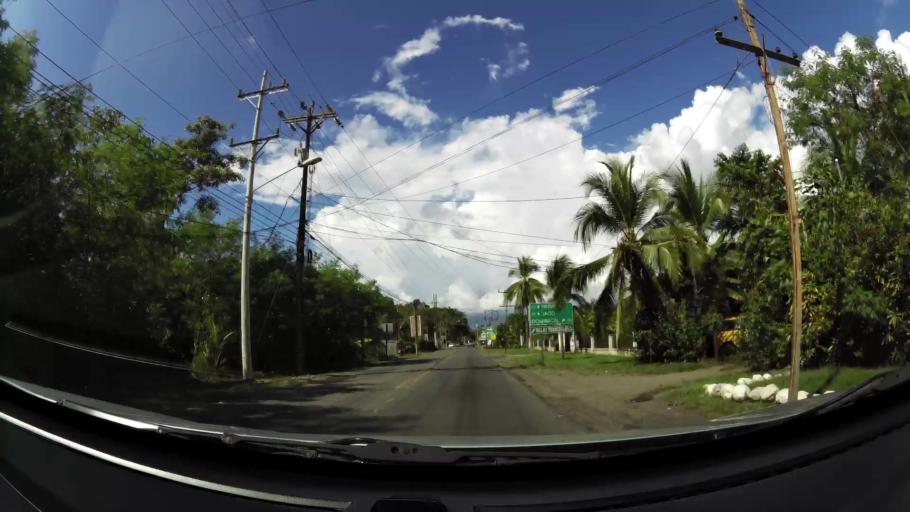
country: CR
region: Puntarenas
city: Quepos
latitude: 9.4488
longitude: -84.1665
